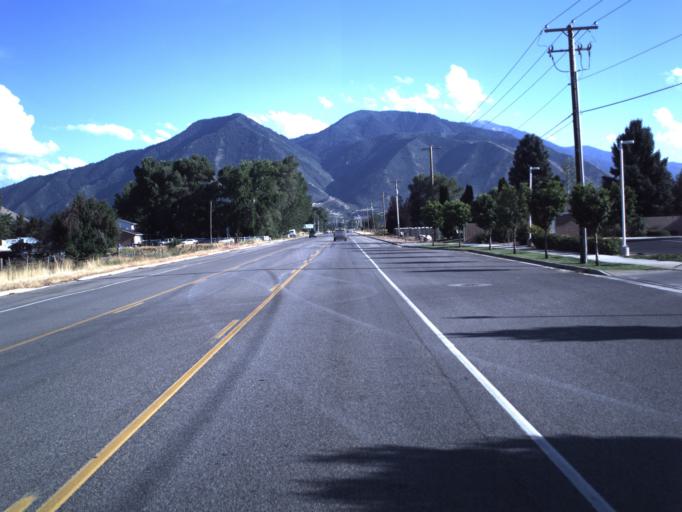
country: US
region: Utah
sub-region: Utah County
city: Mapleton
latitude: 40.1208
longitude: -111.5978
